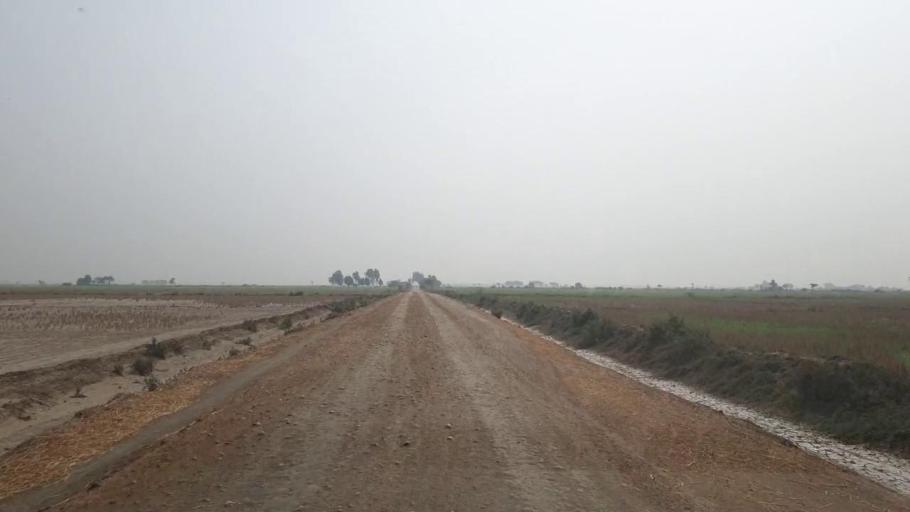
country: PK
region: Sindh
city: Kario
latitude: 24.6364
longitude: 68.5958
